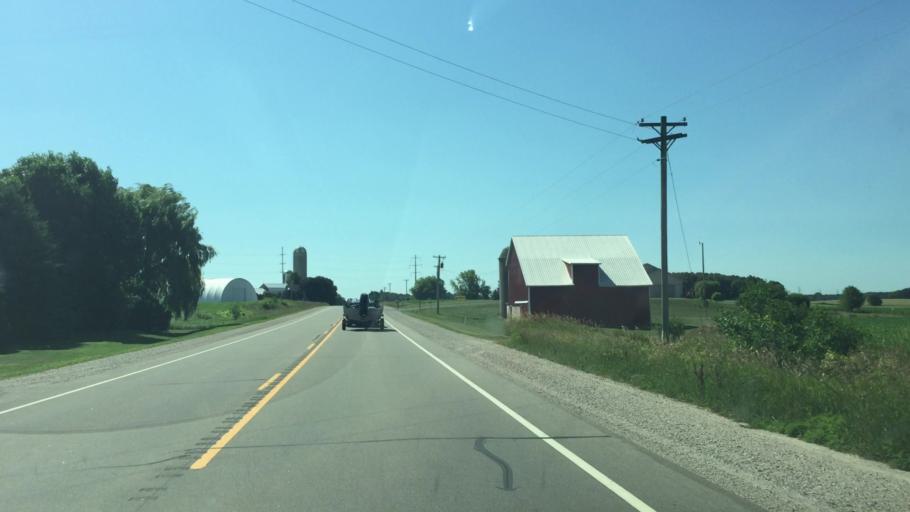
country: US
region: Wisconsin
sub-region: Calumet County
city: Chilton
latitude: 44.0029
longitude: -88.1358
